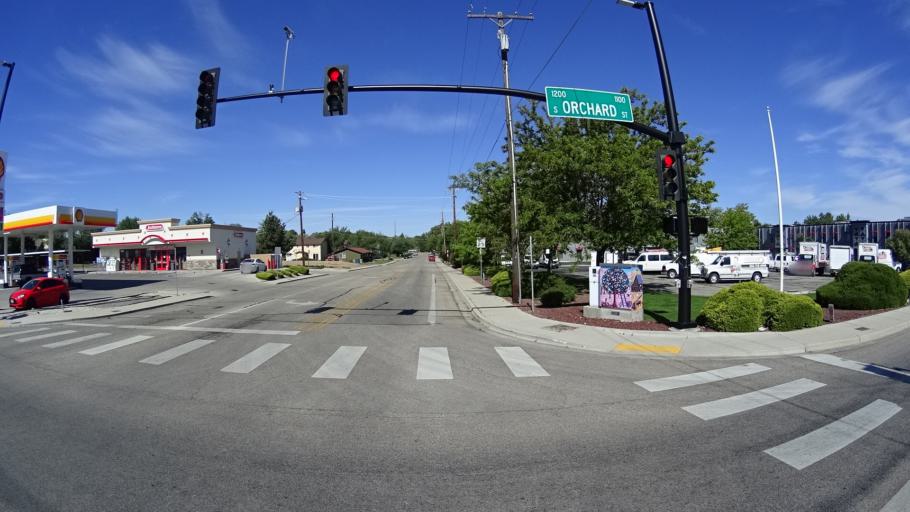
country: US
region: Idaho
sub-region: Ada County
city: Garden City
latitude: 43.5935
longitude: -116.2436
